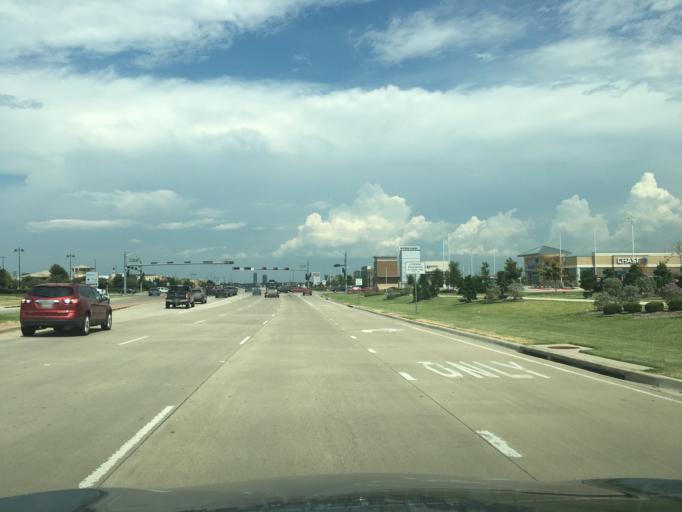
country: US
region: Texas
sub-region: Denton County
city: Denton
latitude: 33.2298
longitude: -97.1709
